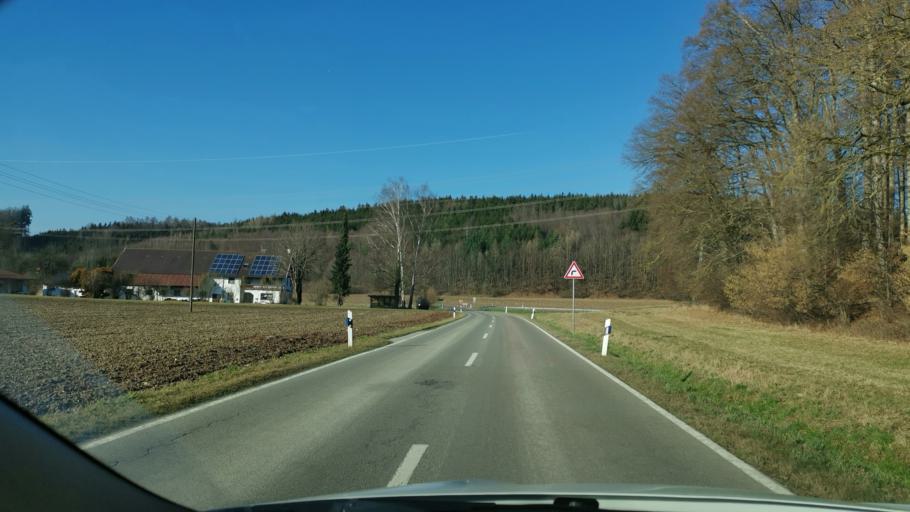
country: DE
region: Bavaria
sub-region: Swabia
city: Rehling
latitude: 48.4936
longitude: 10.9450
